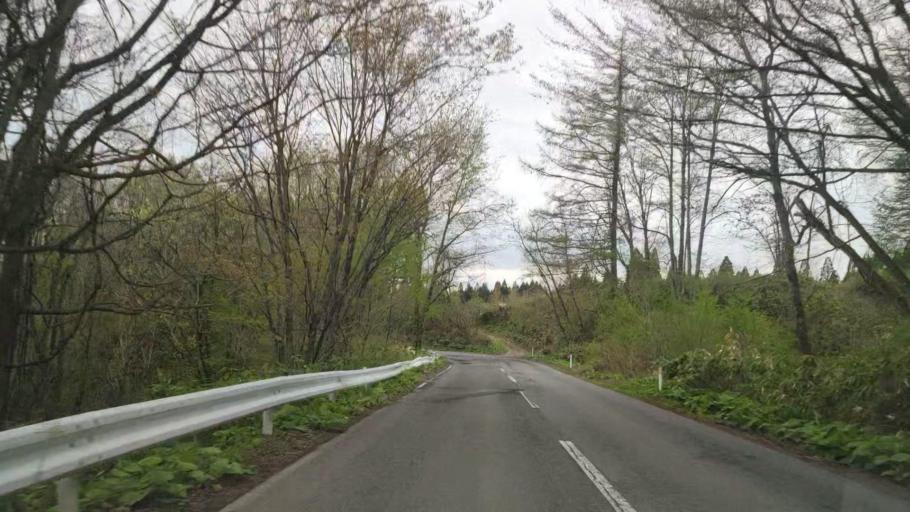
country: JP
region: Akita
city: Hanawa
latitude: 40.3768
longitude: 140.7899
